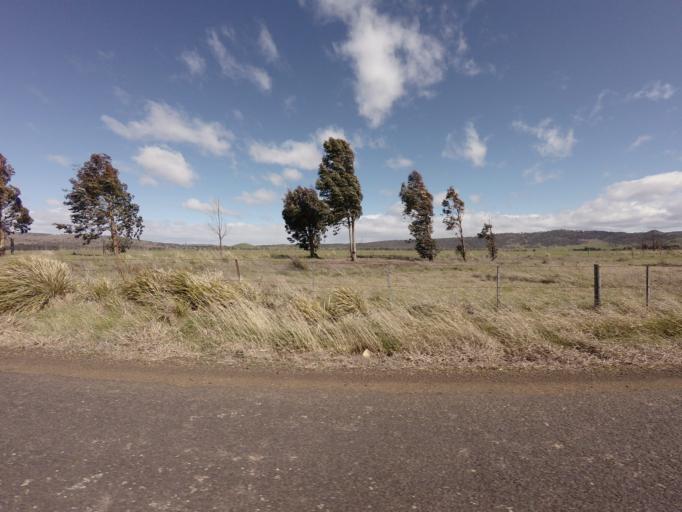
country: AU
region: Tasmania
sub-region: Northern Midlands
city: Evandale
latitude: -42.0142
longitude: 147.4614
